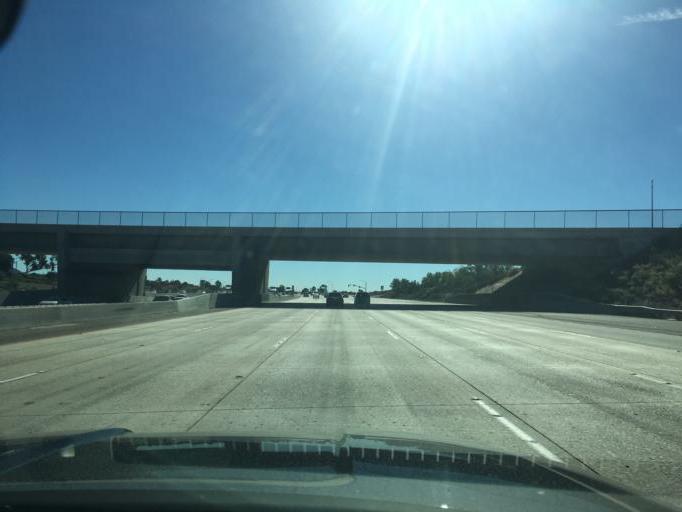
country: US
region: California
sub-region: San Diego County
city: Poway
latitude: 32.8943
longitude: -117.1158
